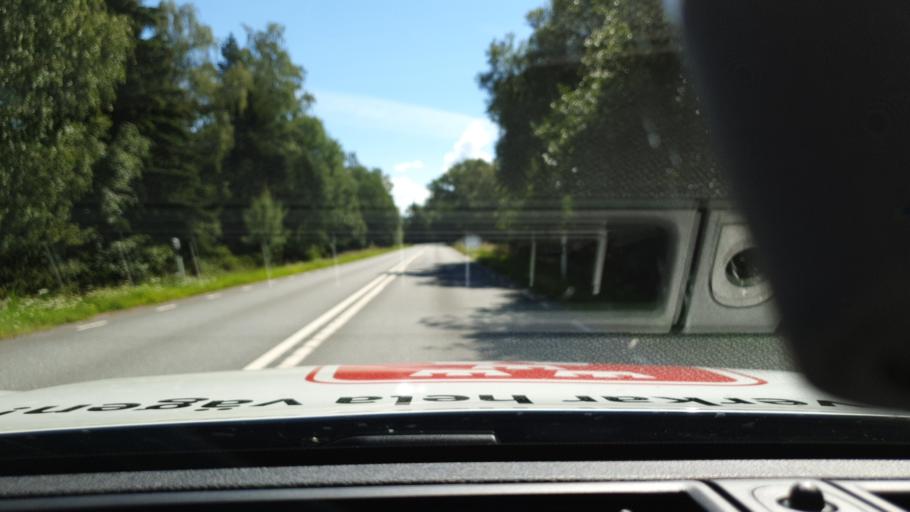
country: SE
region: Joenkoeping
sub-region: Jonkopings Kommun
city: Asa
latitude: 58.0036
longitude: 14.6059
